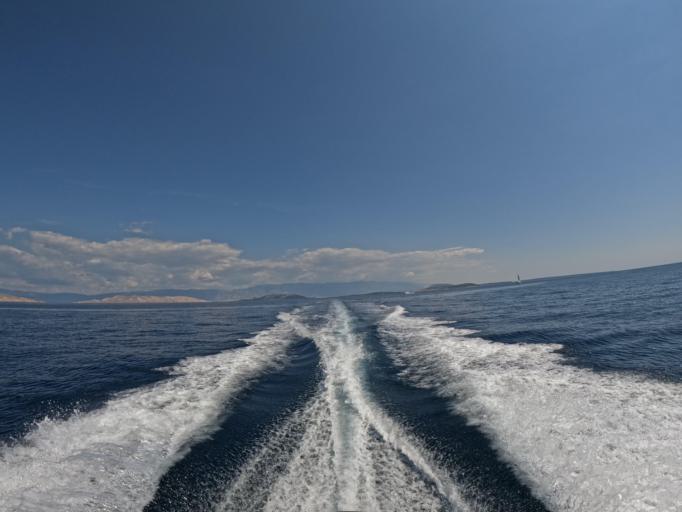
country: HR
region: Primorsko-Goranska
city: Punat
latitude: 44.8944
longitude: 14.6243
